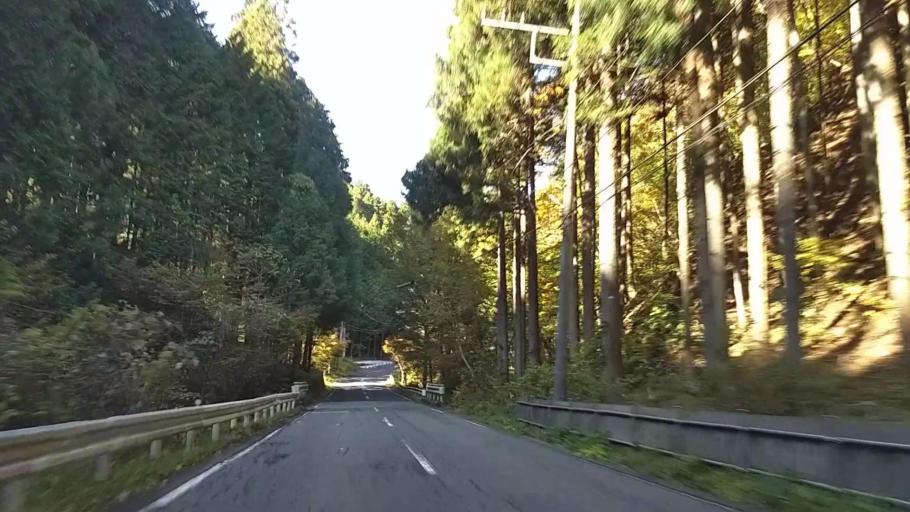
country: JP
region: Yamanashi
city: Otsuki
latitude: 35.7381
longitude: 138.9693
